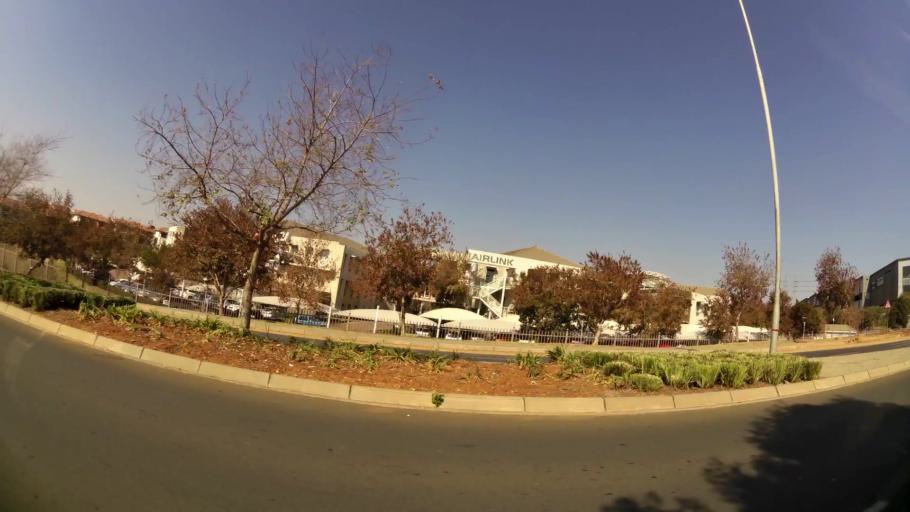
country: ZA
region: Gauteng
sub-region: City of Johannesburg Metropolitan Municipality
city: Modderfontein
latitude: -26.1159
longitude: 28.1473
